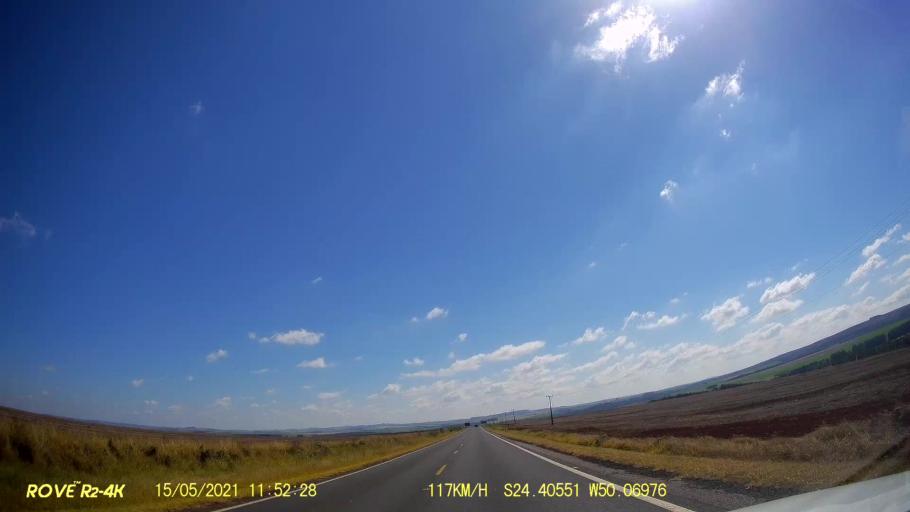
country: BR
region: Parana
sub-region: Pirai Do Sul
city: Pirai do Sul
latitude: -24.4057
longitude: -50.0695
